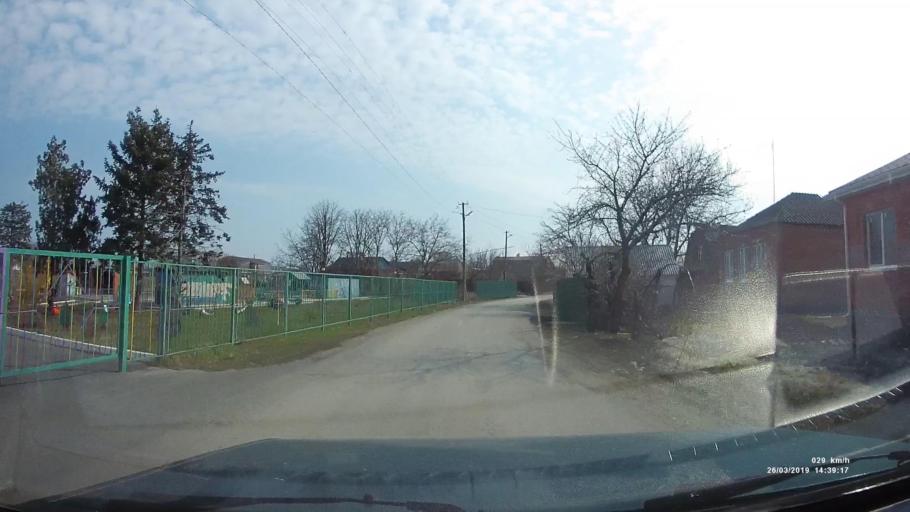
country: RU
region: Rostov
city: Novobessergenovka
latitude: 47.1789
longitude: 38.8628
